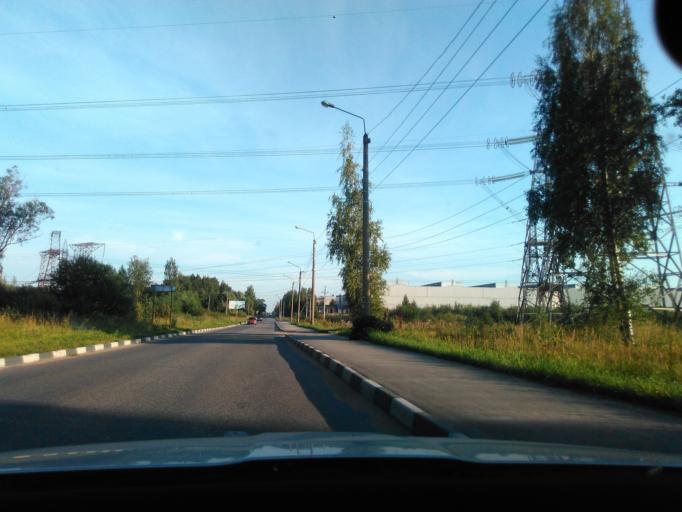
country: RU
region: Tverskaya
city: Konakovo
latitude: 56.7287
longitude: 36.7812
